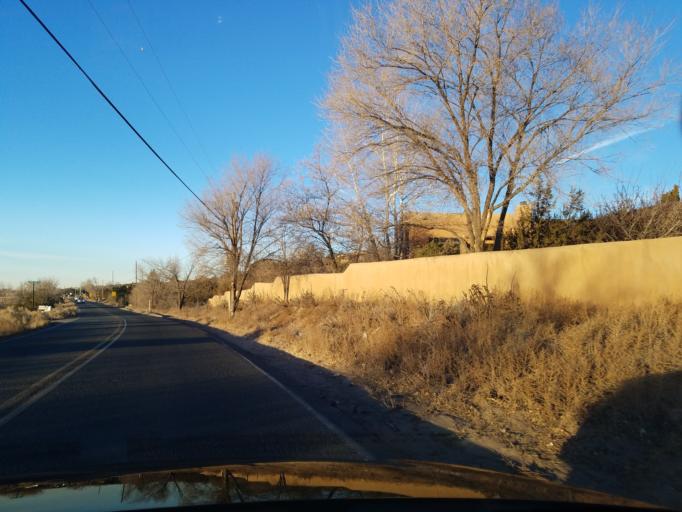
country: US
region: New Mexico
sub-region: Santa Fe County
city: Agua Fria
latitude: 35.6717
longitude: -105.9953
